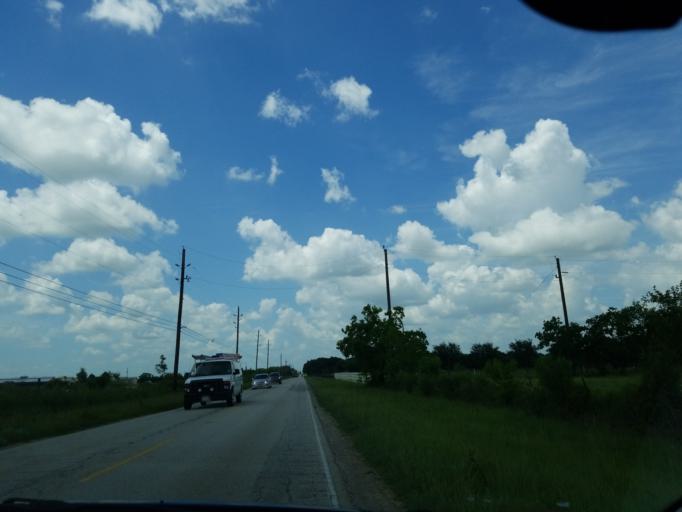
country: US
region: Texas
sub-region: Harris County
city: Katy
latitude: 29.8543
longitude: -95.8069
